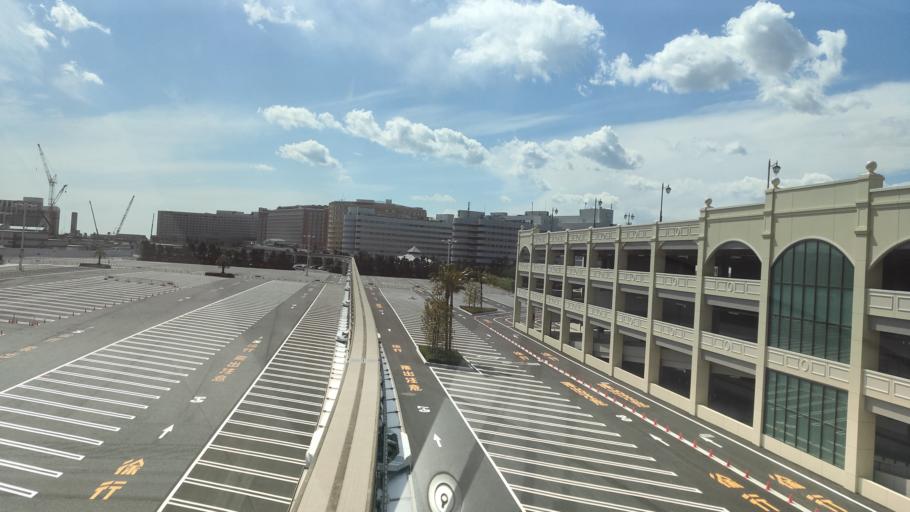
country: JP
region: Tokyo
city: Urayasu
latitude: 35.6348
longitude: 139.8762
